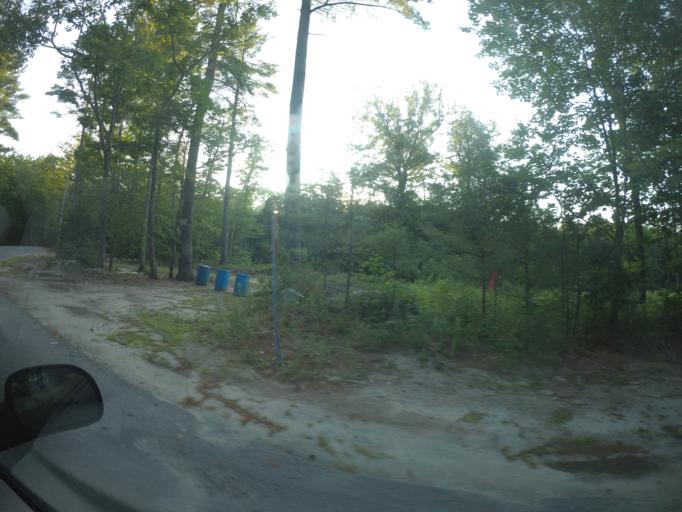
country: US
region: Maine
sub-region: Cumberland County
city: Raymond
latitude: 43.8887
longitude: -70.4170
